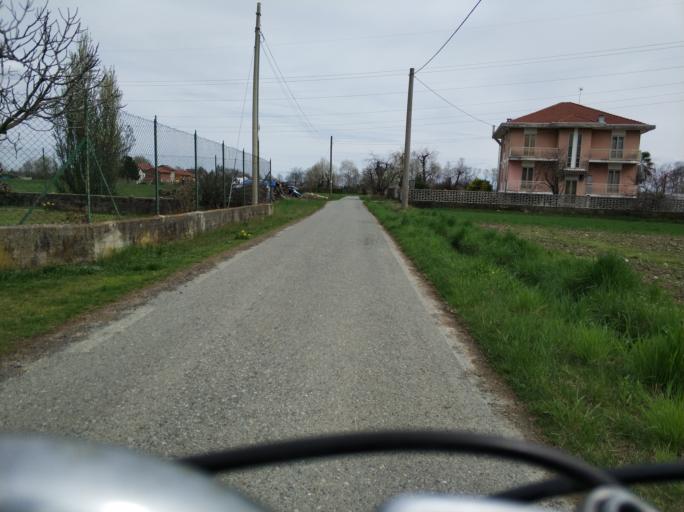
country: IT
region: Piedmont
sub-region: Provincia di Torino
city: Nole
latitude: 45.2326
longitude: 7.5696
